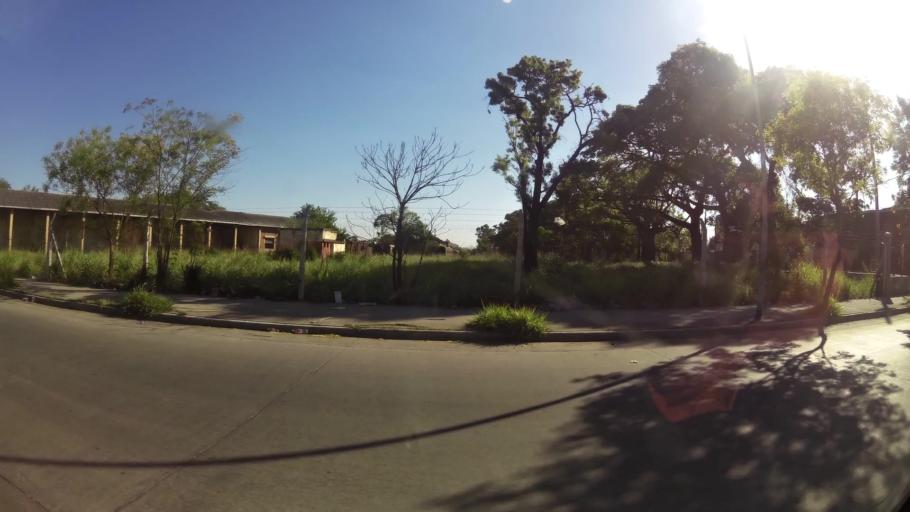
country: AR
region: Cordoba
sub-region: Departamento de Capital
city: Cordoba
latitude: -31.3939
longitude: -64.1650
